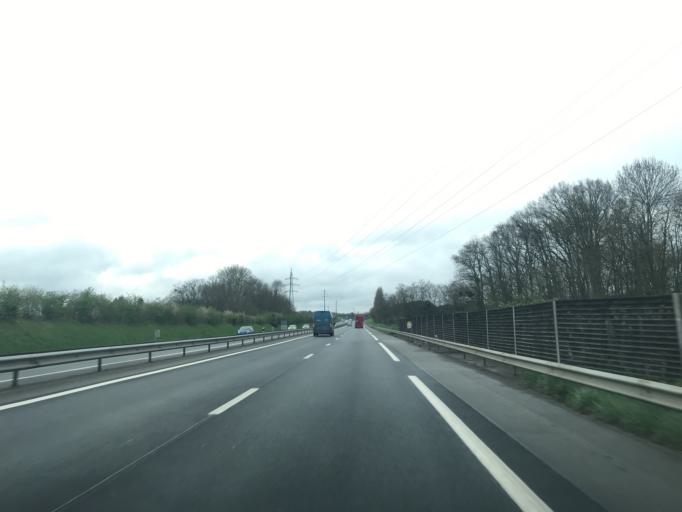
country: FR
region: Centre
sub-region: Departement du Loiret
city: Checy
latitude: 47.9129
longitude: 2.0223
